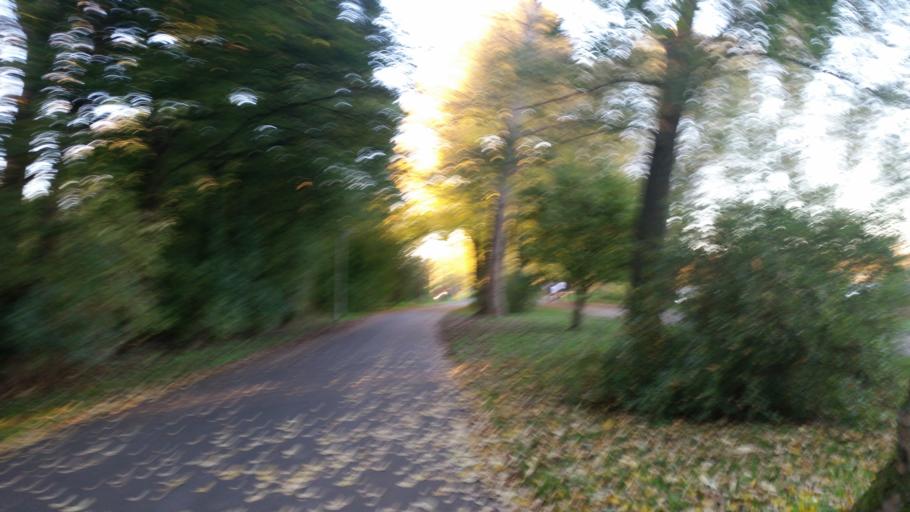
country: DE
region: Lower Saxony
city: Hannover
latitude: 52.3475
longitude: 9.7443
